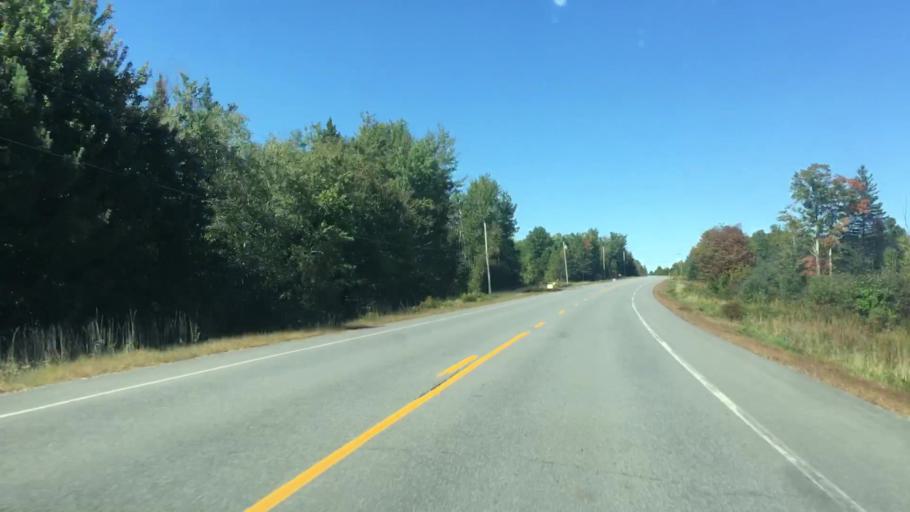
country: US
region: Maine
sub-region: Piscataquis County
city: Sangerville
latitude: 45.0694
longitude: -69.4589
